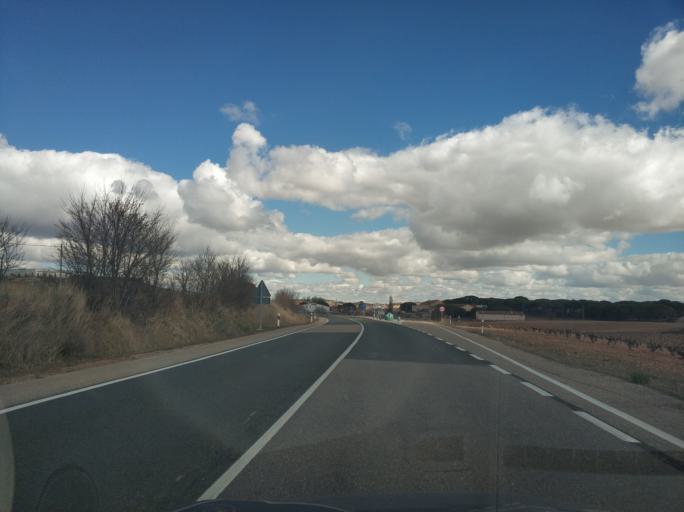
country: ES
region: Castille and Leon
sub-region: Provincia de Burgos
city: Fuentecen
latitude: 41.6249
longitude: -3.8826
